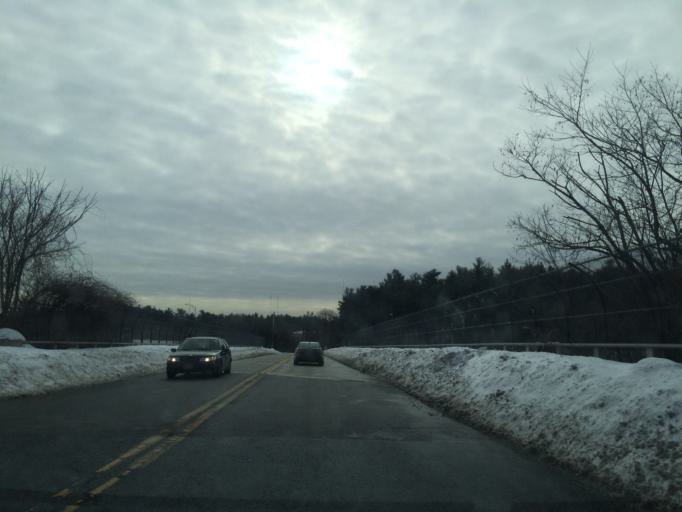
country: US
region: Massachusetts
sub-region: Middlesex County
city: Weston
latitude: 42.3393
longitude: -71.2688
